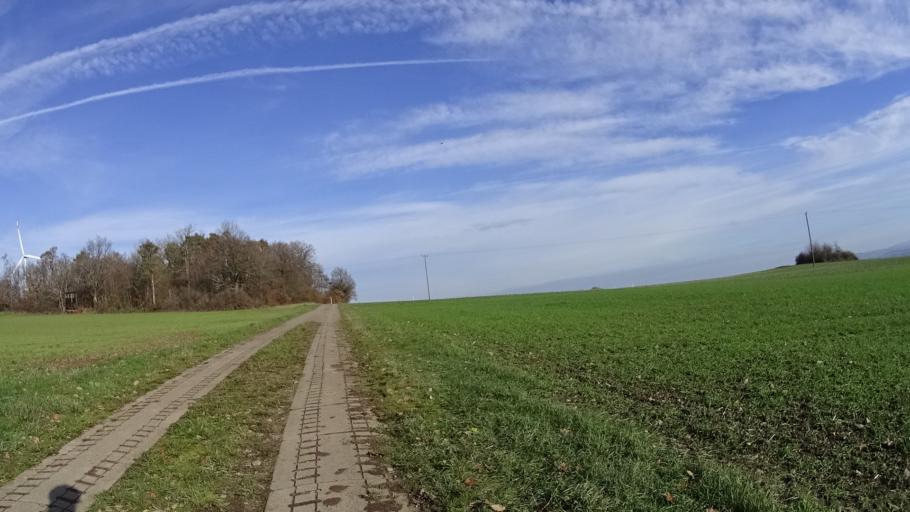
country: DE
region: Rheinland-Pfalz
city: Kirrweiler
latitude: 49.6405
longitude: 7.4934
